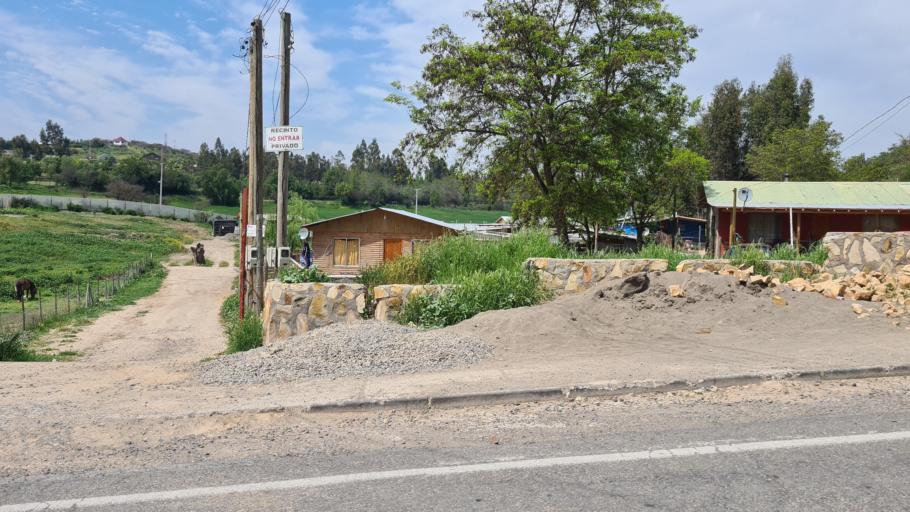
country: CL
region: O'Higgins
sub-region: Provincia de Cachapoal
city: San Vicente
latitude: -34.1596
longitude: -71.4266
